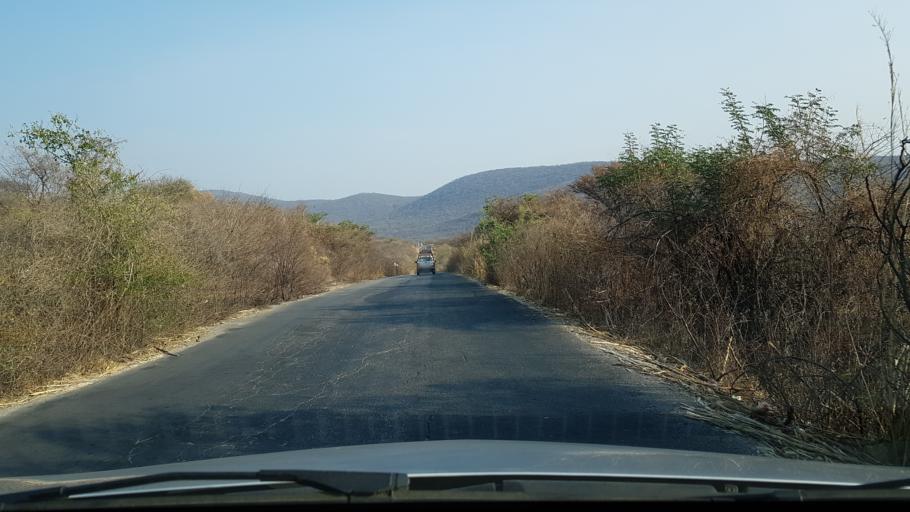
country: MX
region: Morelos
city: Tlaltizapan
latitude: 18.6661
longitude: -99.0524
